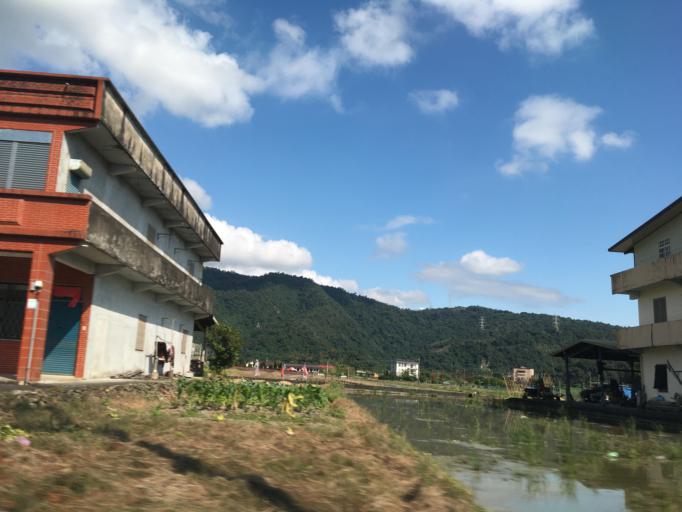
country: TW
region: Taiwan
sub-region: Yilan
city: Yilan
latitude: 24.7463
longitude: 121.6937
